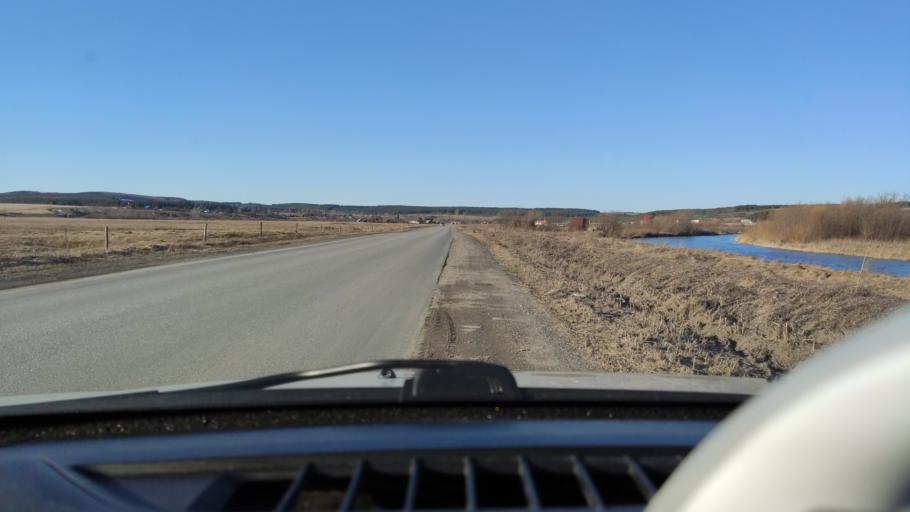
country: RU
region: Perm
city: Suksun
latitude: 57.0443
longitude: 57.4231
